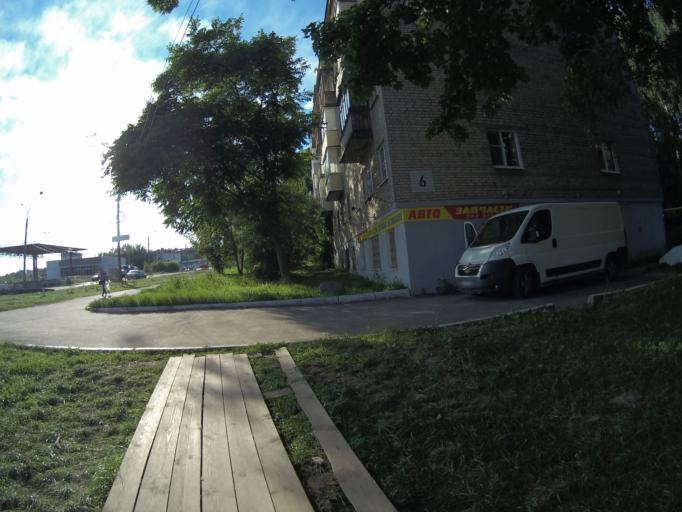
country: RU
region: Vladimir
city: Kommunar
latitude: 56.1383
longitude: 40.4291
